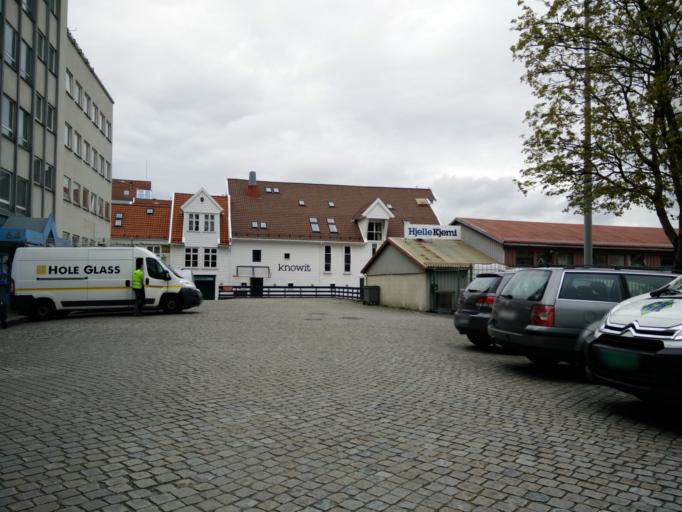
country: NO
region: Hordaland
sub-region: Bergen
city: Bergen
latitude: 60.3993
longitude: 5.3092
